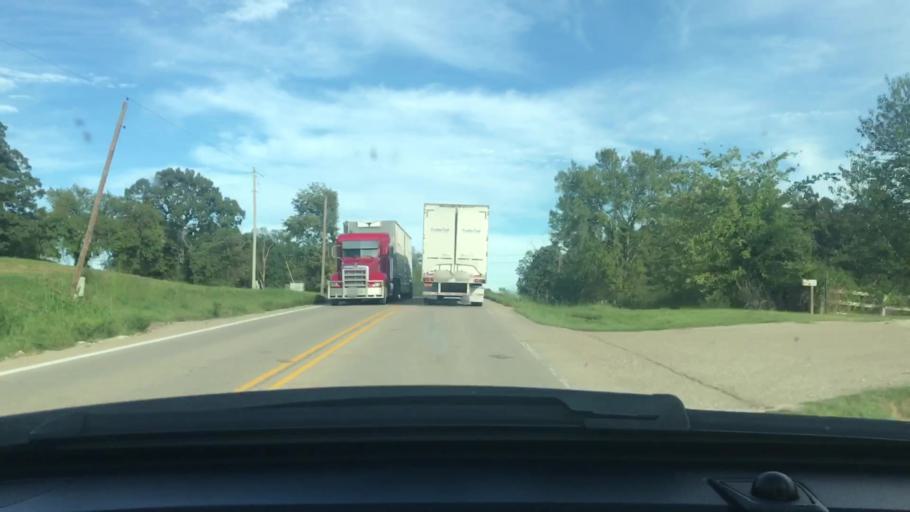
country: US
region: Arkansas
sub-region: Sharp County
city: Cherokee Village
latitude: 36.2395
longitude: -91.2619
